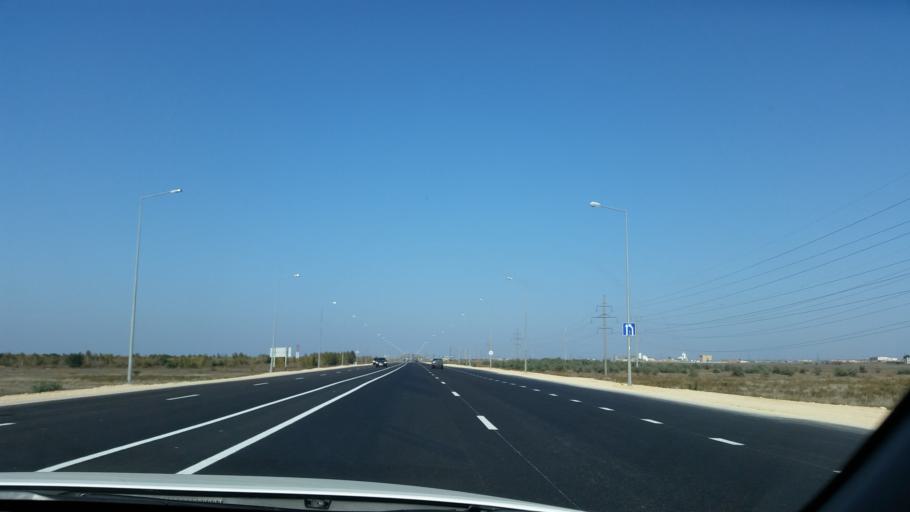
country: KZ
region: Astana Qalasy
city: Astana
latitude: 51.2103
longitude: 71.3151
